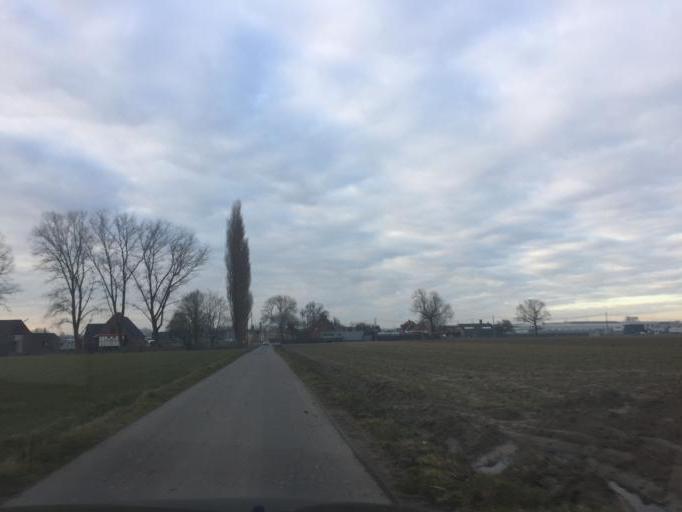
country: BE
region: Flanders
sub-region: Provincie West-Vlaanderen
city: Roeselare
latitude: 50.9847
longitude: 3.1320
